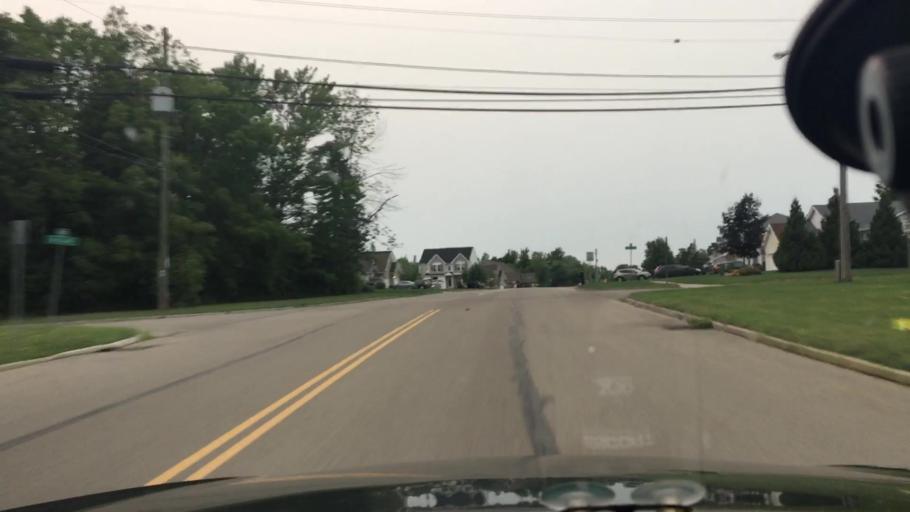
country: US
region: New York
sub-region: Erie County
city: Blasdell
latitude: 42.7743
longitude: -78.8049
